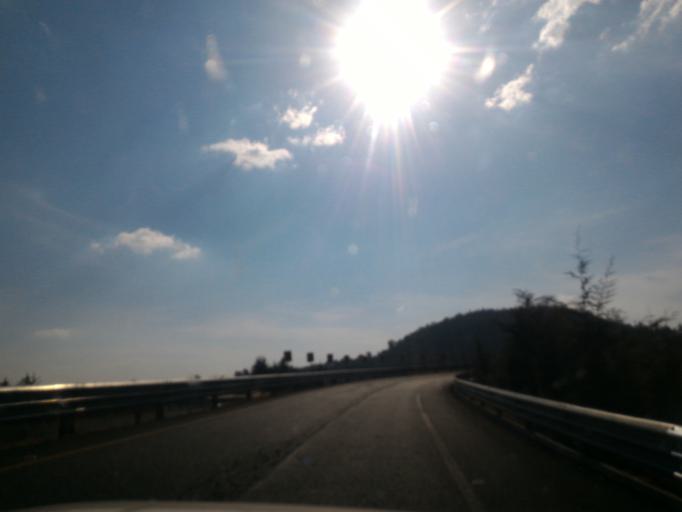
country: MX
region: Mexico
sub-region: Atlacomulco
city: San Luis Boro
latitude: 19.8326
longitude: -99.8709
